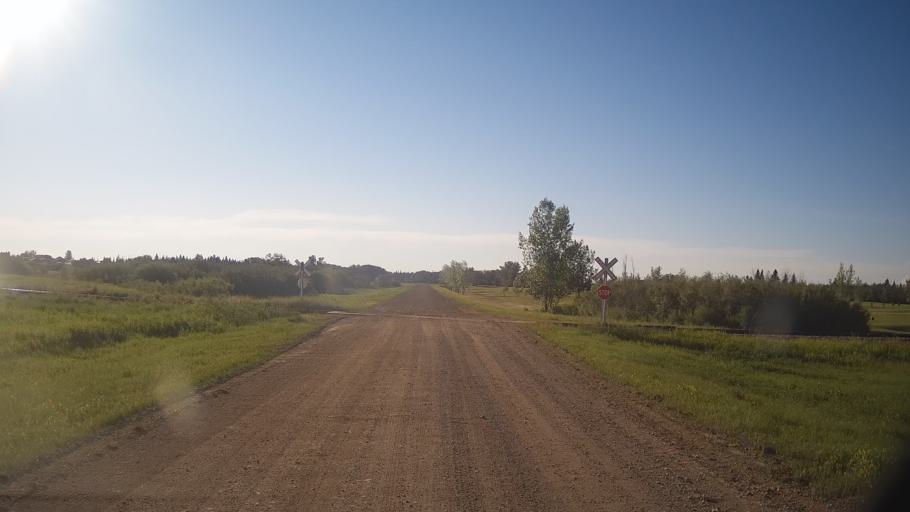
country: CA
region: Saskatchewan
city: Lanigan
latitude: 51.8481
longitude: -105.0123
